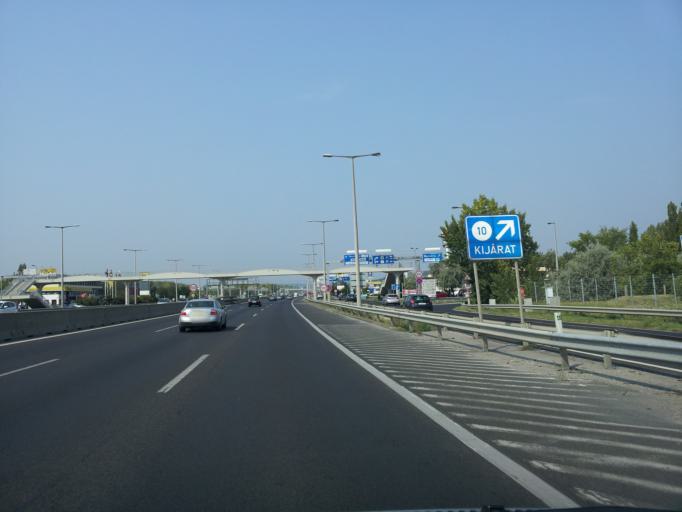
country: HU
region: Pest
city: Budaors
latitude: 47.4526
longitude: 18.9607
